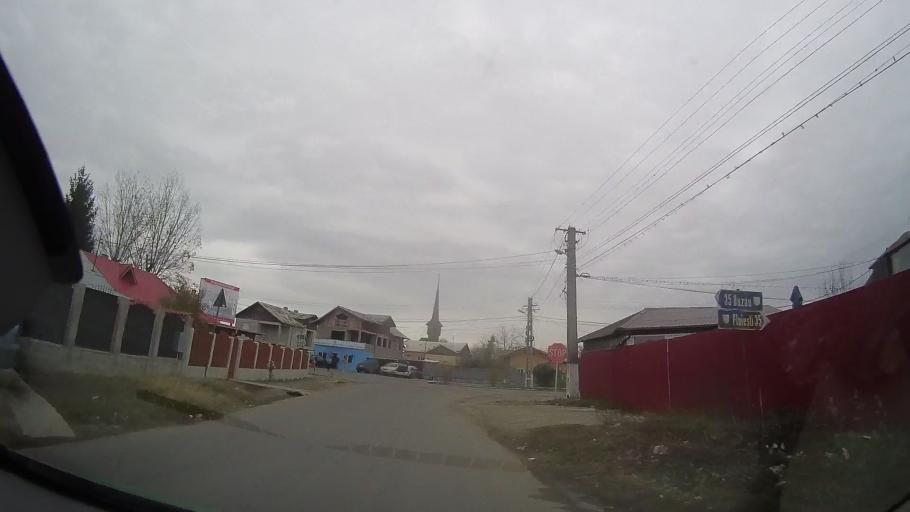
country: RO
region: Prahova
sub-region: Oras Mizil
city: Mizil
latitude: 45.0005
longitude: 26.4336
